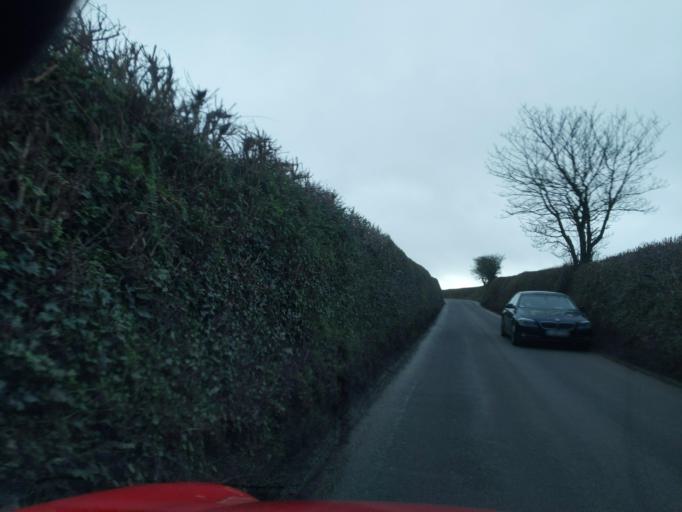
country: GB
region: England
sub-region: Plymouth
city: Plymstock
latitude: 50.3392
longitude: -4.0958
